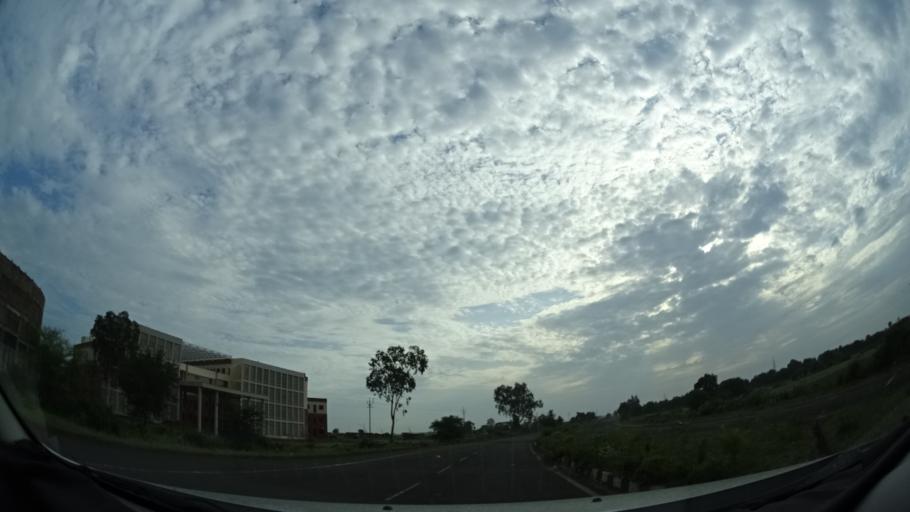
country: IN
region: Madhya Pradesh
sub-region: Bhopal
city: Bhopal
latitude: 23.2830
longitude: 77.2806
